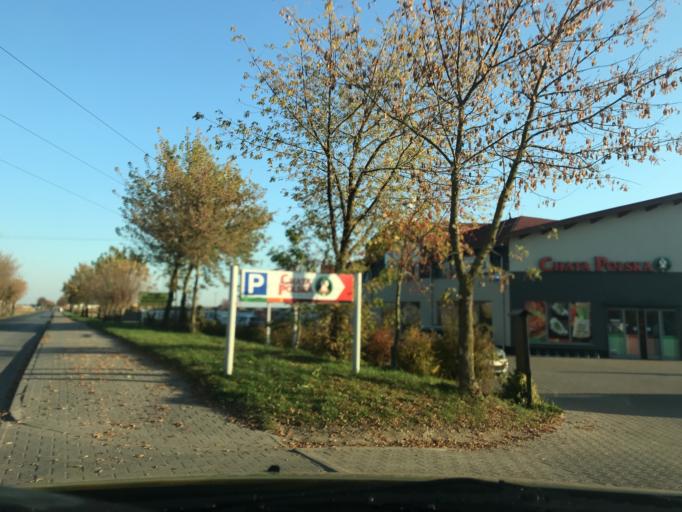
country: PL
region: Greater Poland Voivodeship
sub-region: Powiat poznanski
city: Baranowo
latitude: 52.3972
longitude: 16.7570
